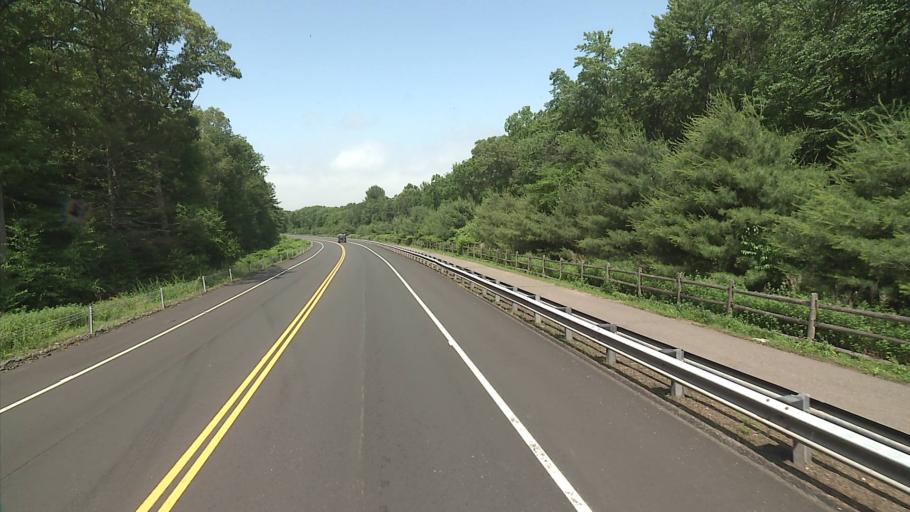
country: US
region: Connecticut
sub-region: Hartford County
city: Manchester
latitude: 41.7167
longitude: -72.5343
